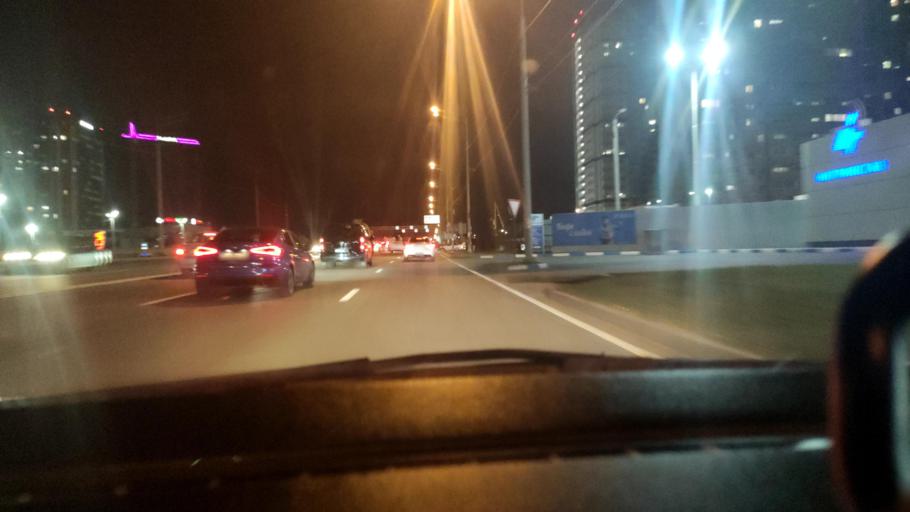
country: RU
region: Voronezj
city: Podgornoye
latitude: 51.7167
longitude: 39.1446
